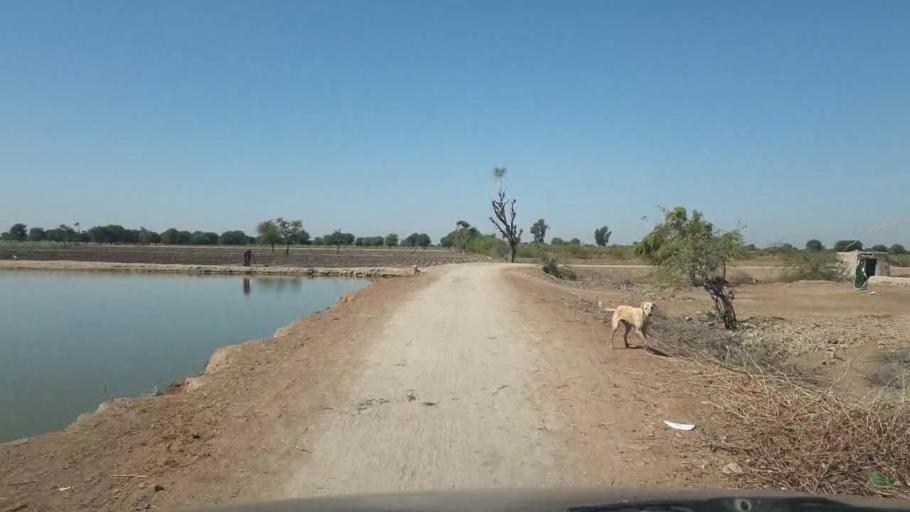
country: PK
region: Sindh
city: Umarkot
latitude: 25.4192
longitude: 69.6459
